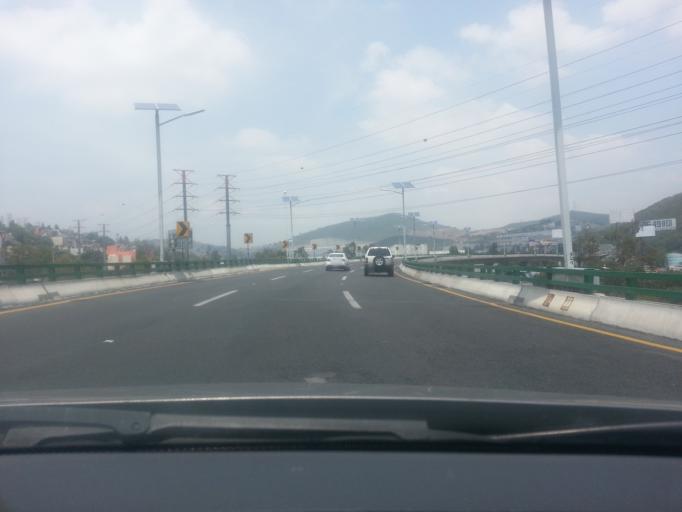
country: MX
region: Mexico
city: Tlalnepantla
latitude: 19.5670
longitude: -99.2085
